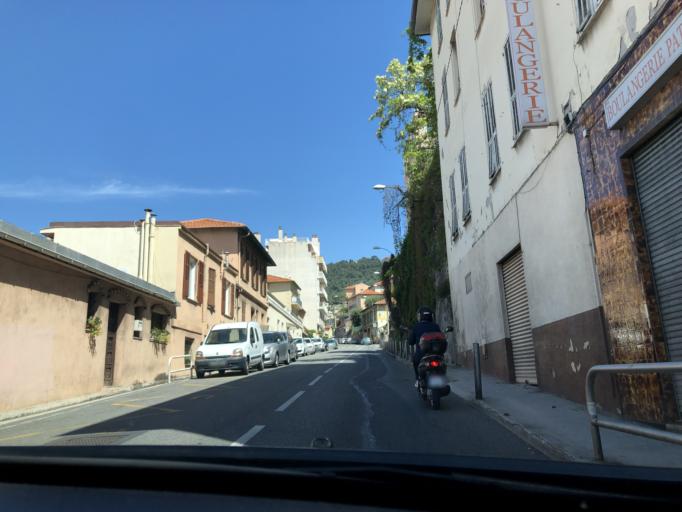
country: FR
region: Provence-Alpes-Cote d'Azur
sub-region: Departement des Alpes-Maritimes
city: Villefranche-sur-Mer
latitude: 43.7111
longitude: 7.2953
